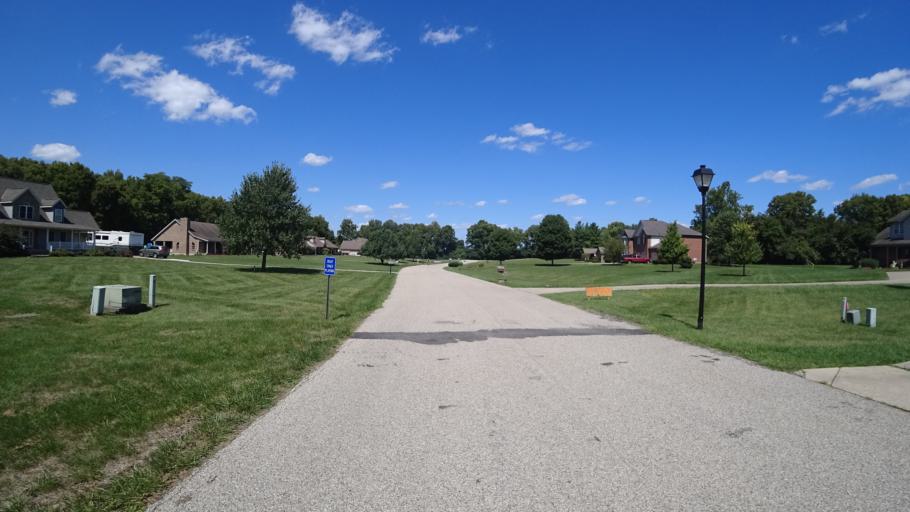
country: US
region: Ohio
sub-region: Butler County
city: New Miami
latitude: 39.4138
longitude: -84.5266
